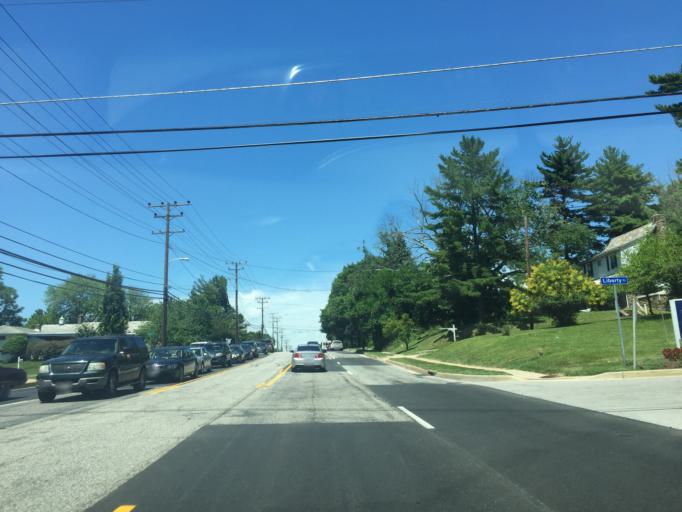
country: US
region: Maryland
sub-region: Baltimore County
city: Milford Mill
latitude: 39.3581
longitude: -76.7698
